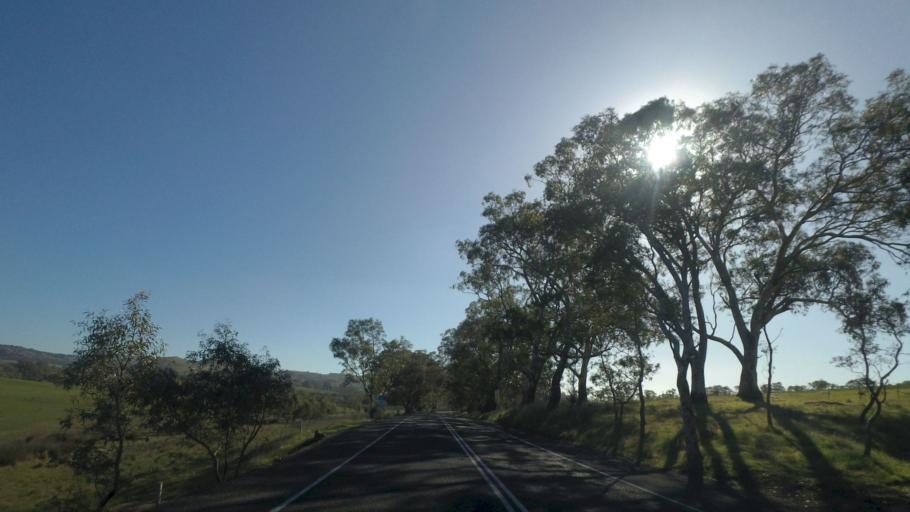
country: AU
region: Victoria
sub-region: Mount Alexander
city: Castlemaine
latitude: -36.9517
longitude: 144.3410
